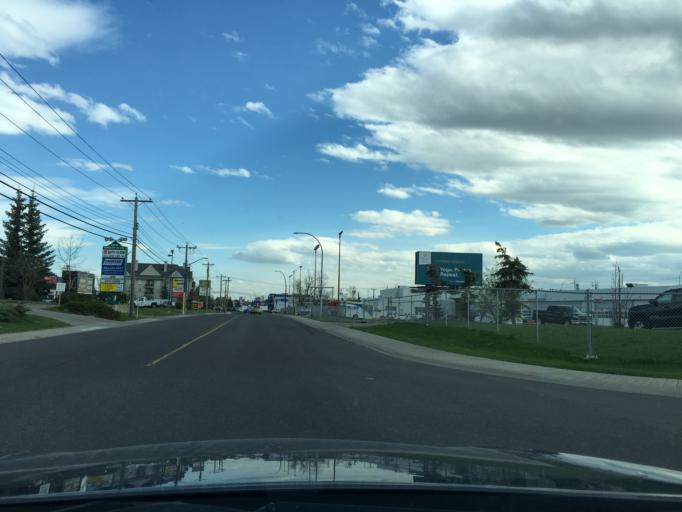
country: CA
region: Alberta
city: Calgary
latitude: 50.9191
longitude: -114.0686
